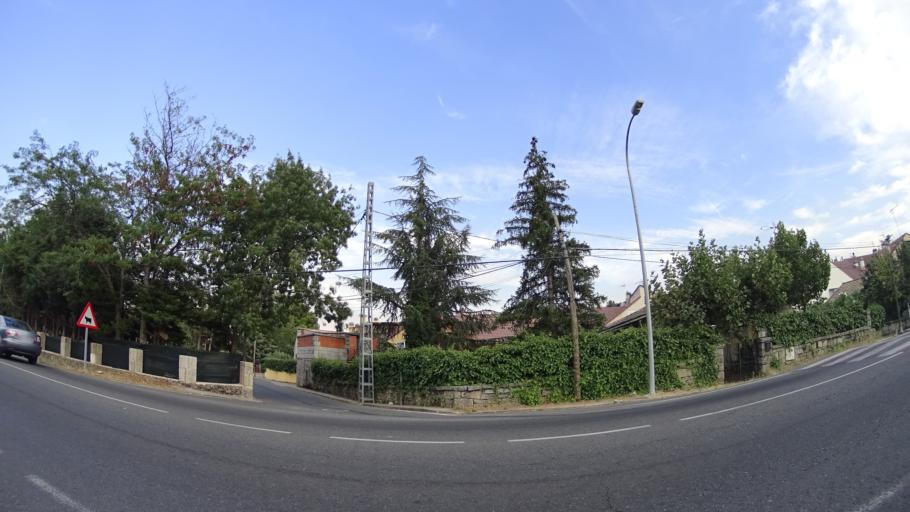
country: ES
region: Madrid
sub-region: Provincia de Madrid
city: Becerril de la Sierra
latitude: 40.7070
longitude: -3.9948
